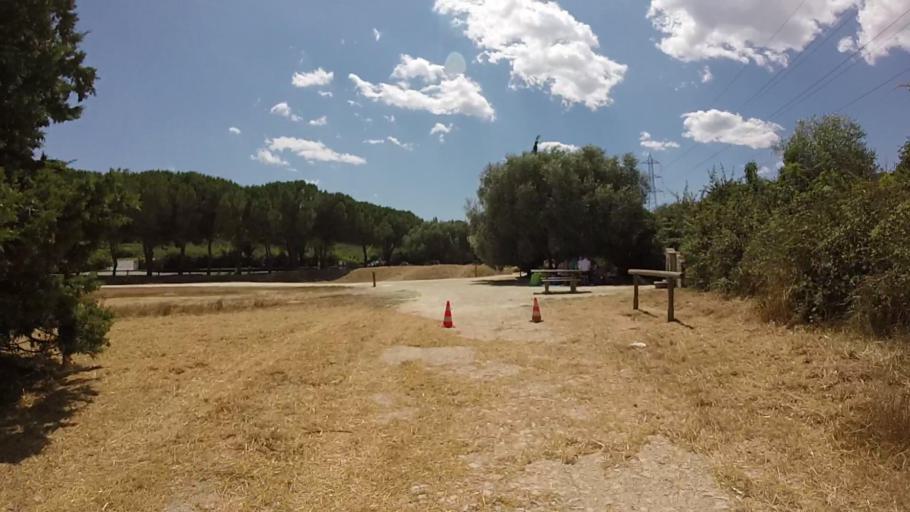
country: FR
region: Provence-Alpes-Cote d'Azur
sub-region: Departement des Alpes-Maritimes
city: Mougins
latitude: 43.5946
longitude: 7.0083
